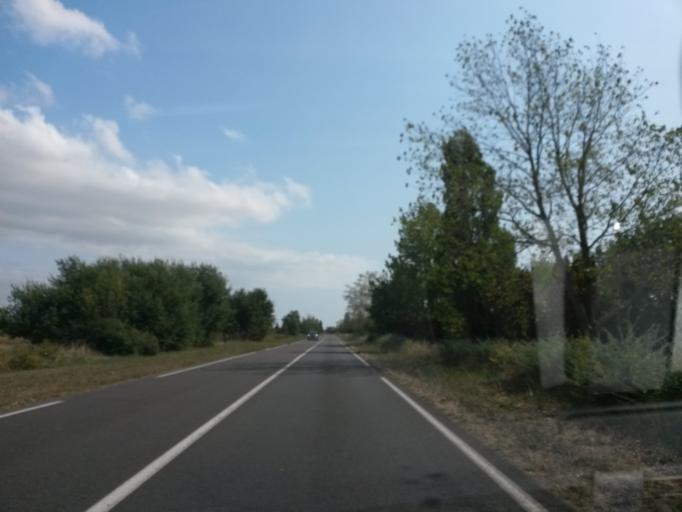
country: FR
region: Pays de la Loire
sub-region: Departement de la Vendee
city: La Tranche-sur-Mer
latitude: 46.3609
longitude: -1.4497
